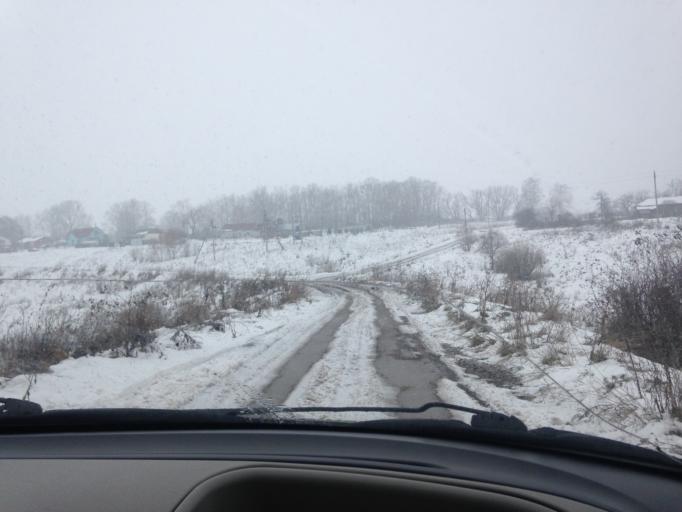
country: RU
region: Tula
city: Shchekino
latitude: 53.8195
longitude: 37.5018
